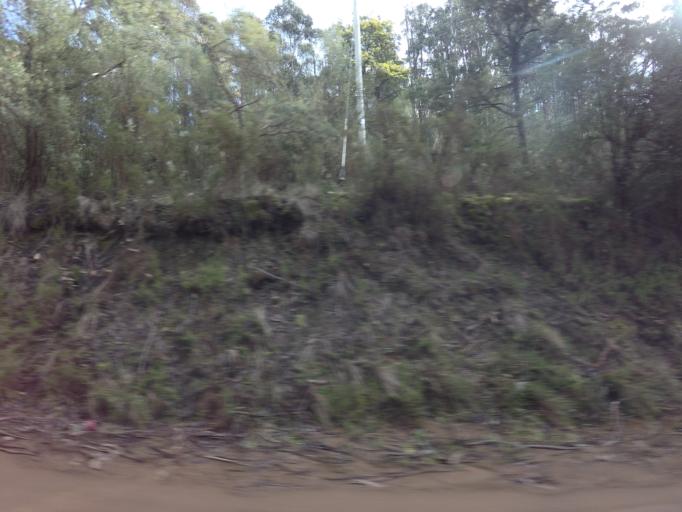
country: AU
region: Tasmania
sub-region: Derwent Valley
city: New Norfolk
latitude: -42.7895
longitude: 146.9333
